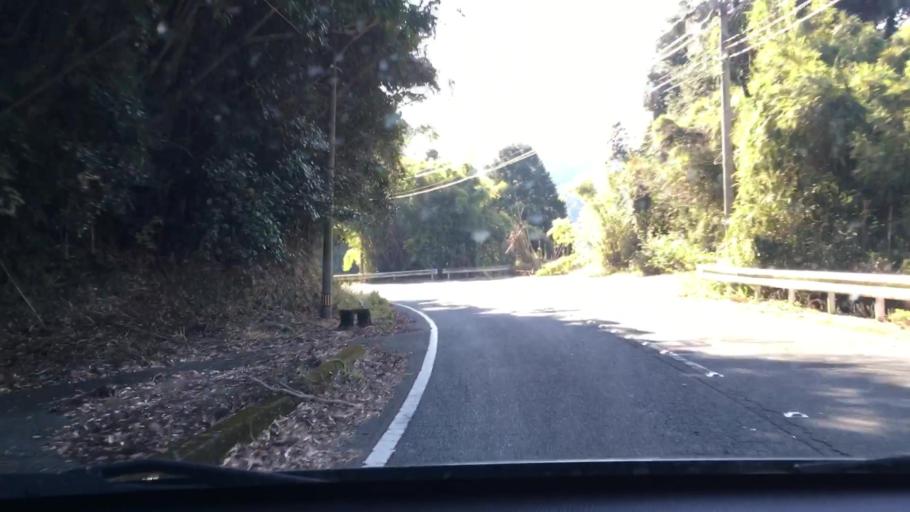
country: JP
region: Kagoshima
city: Kokubu-matsuki
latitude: 31.6706
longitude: 130.8306
